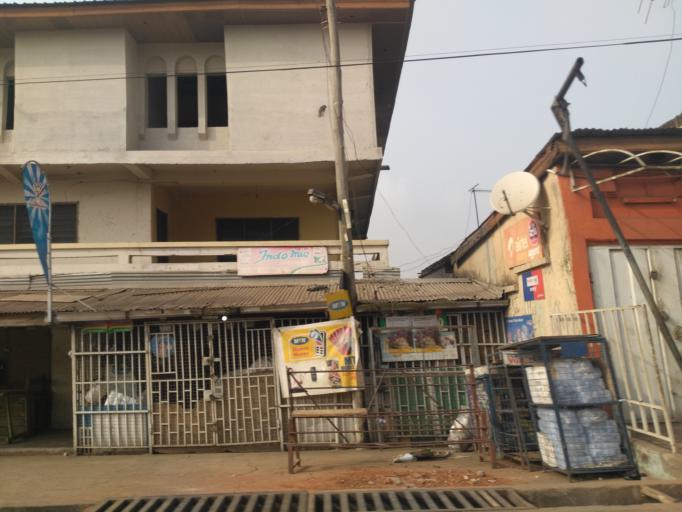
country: GH
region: Ashanti
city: Kumasi
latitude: 6.6996
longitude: -1.5951
